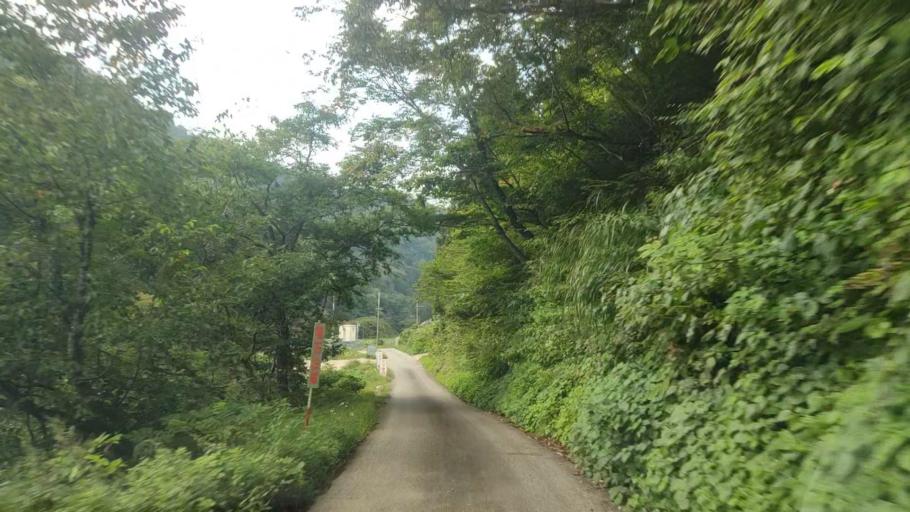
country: JP
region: Toyama
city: Yatsuomachi-higashikumisaka
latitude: 36.4232
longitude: 137.0836
